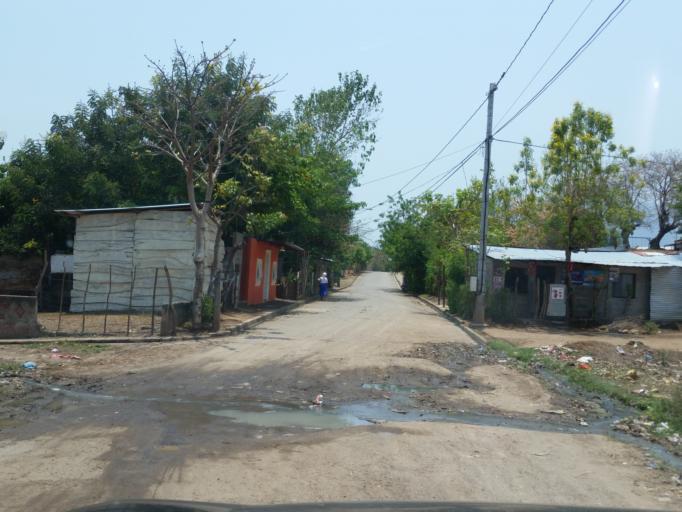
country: NI
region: Granada
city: Granada
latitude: 11.9118
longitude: -85.9538
